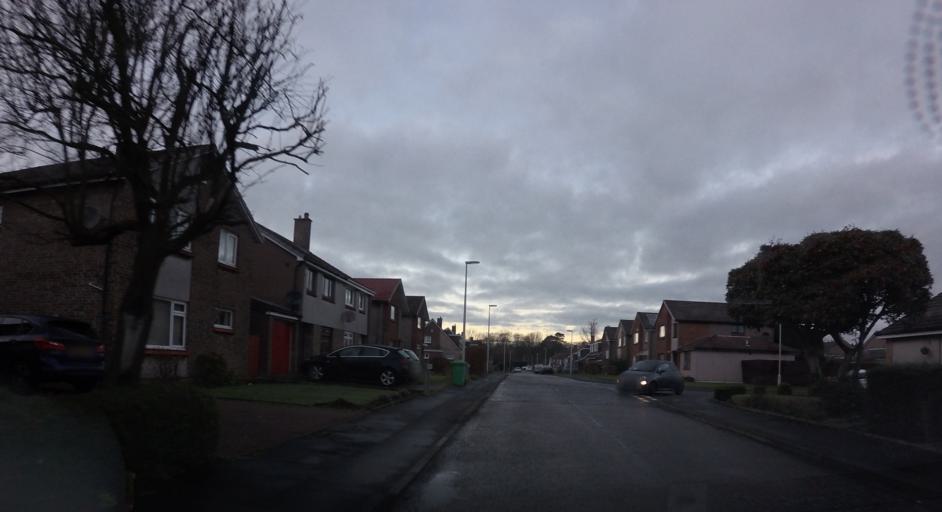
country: GB
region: Scotland
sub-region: Fife
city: Crossford
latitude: 56.0585
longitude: -3.4959
